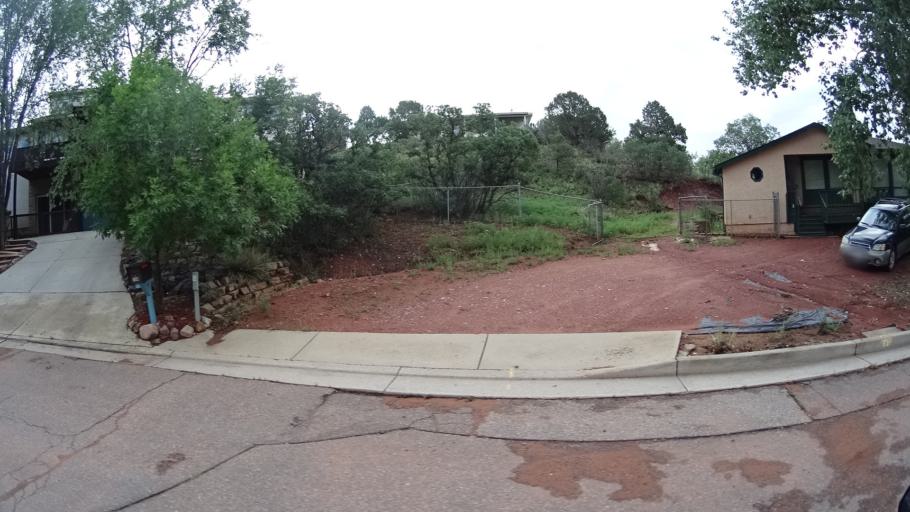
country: US
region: Colorado
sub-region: El Paso County
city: Manitou Springs
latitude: 38.8608
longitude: -104.8940
